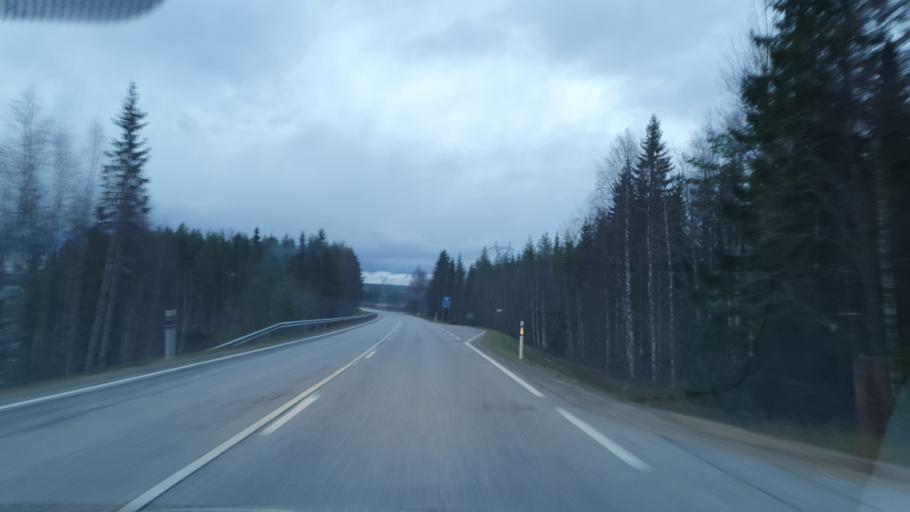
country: FI
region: Kainuu
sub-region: Kehys-Kainuu
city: Hyrynsalmi
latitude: 64.5977
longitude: 28.4506
